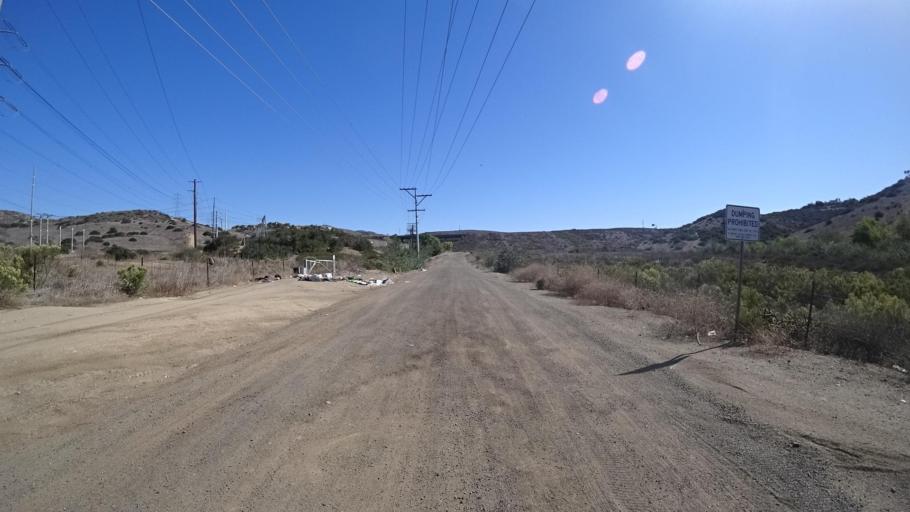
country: US
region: California
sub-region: San Diego County
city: Bonita
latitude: 32.6641
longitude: -116.9881
